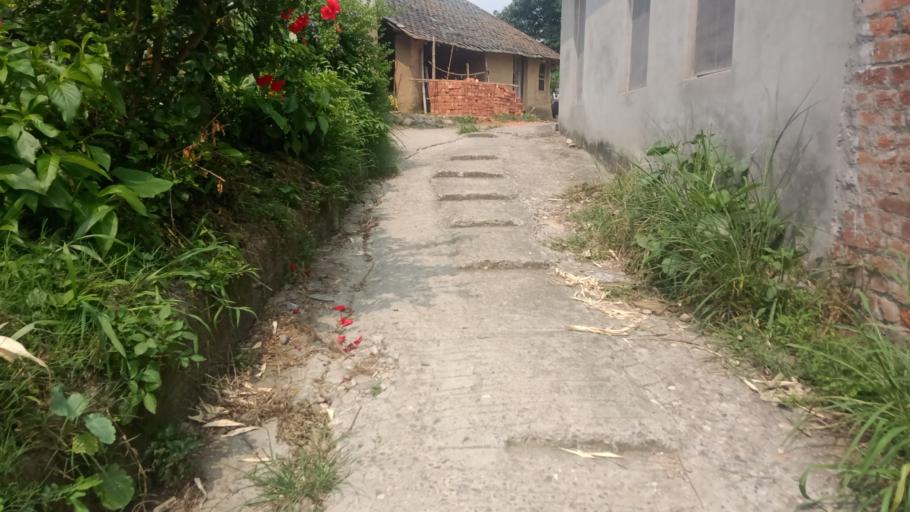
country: IN
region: Himachal Pradesh
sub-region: Hamirpur
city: Nadaun
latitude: 31.6936
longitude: 76.3578
